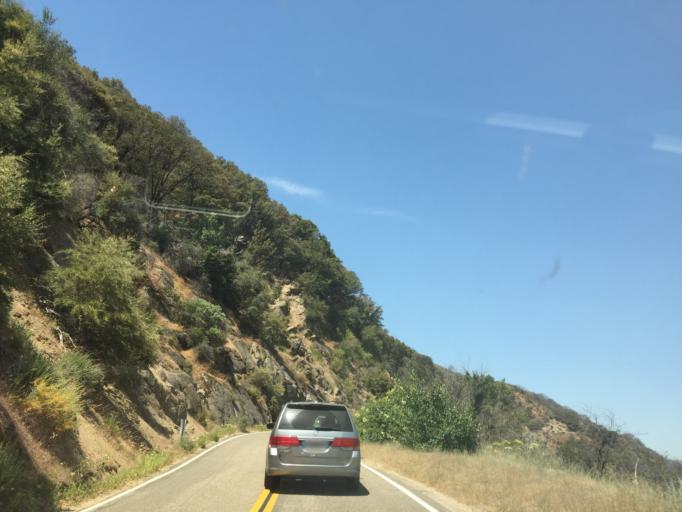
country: US
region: California
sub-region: Fresno County
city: Squaw Valley
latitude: 36.8318
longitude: -118.8922
